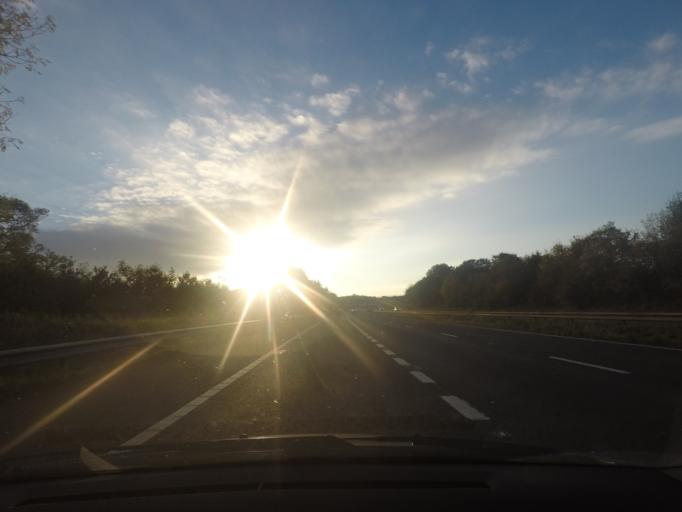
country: GB
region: England
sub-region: North Lincolnshire
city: Scawby
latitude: 53.5453
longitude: -0.5432
